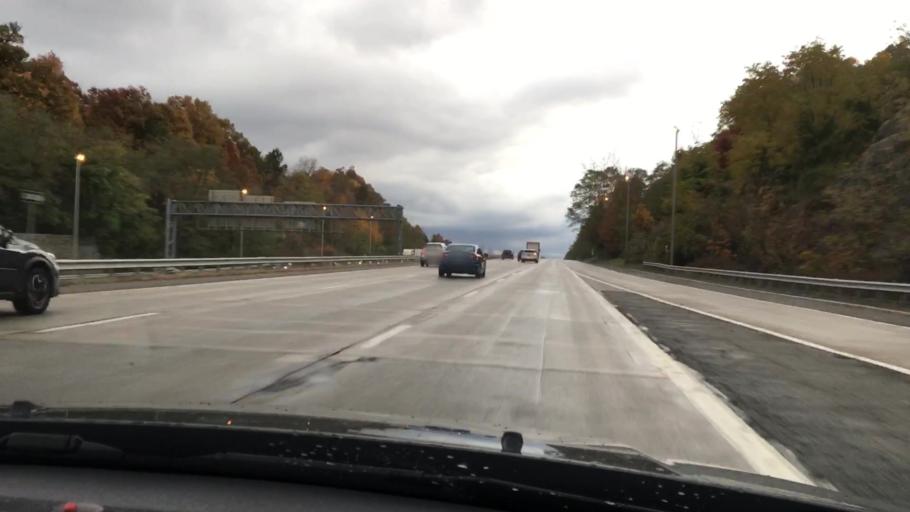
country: US
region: New Jersey
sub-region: Morris County
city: Riverdale
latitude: 40.9860
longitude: -74.3110
